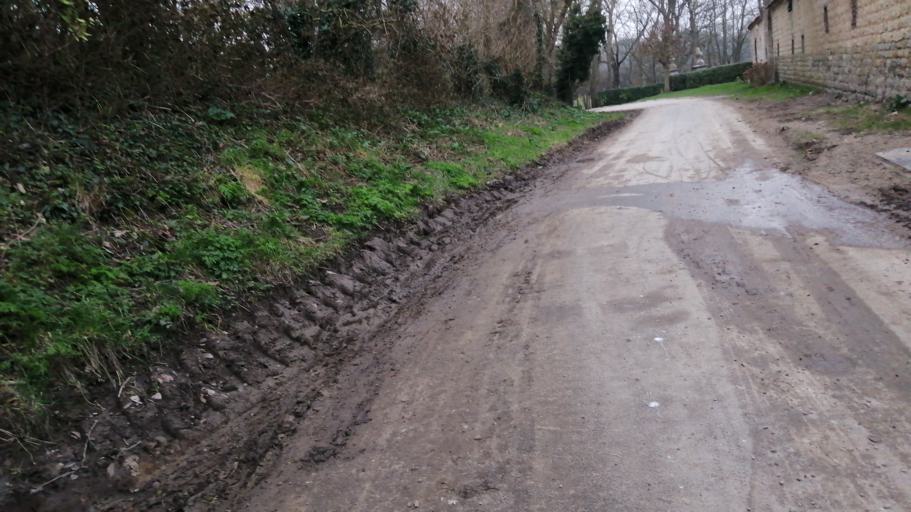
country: FR
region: Nord-Pas-de-Calais
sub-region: Departement du Pas-de-Calais
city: Wissant
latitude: 50.8769
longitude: 1.6820
